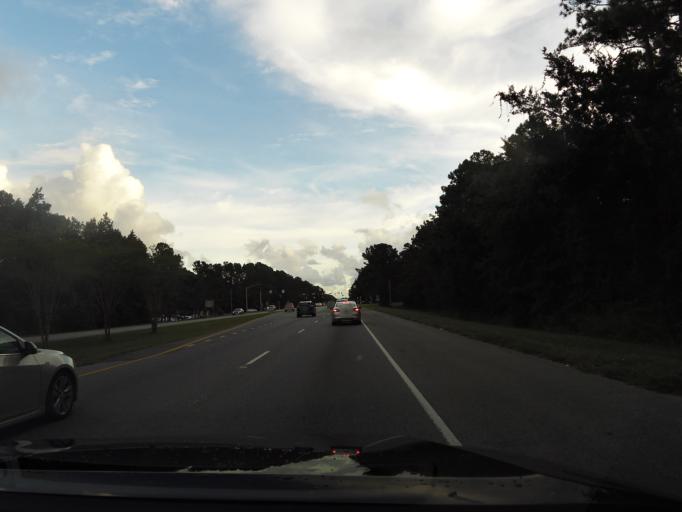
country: US
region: Georgia
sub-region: Glynn County
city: Dock Junction
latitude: 31.2276
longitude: -81.4971
